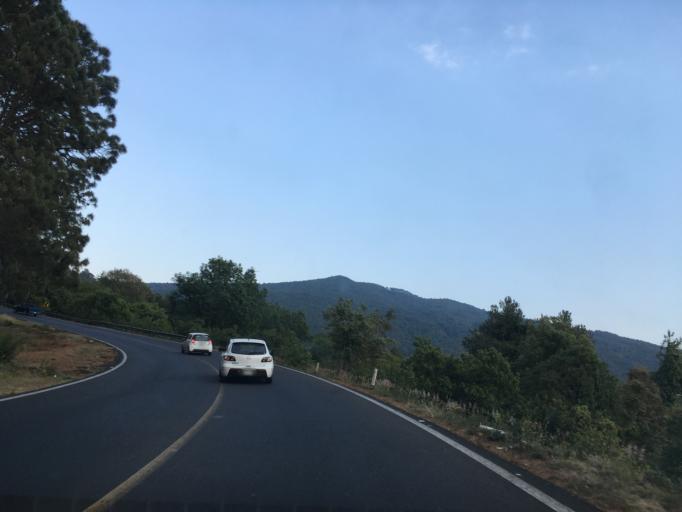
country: MX
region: Michoacan
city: Tingambato
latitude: 19.4924
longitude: -101.8342
